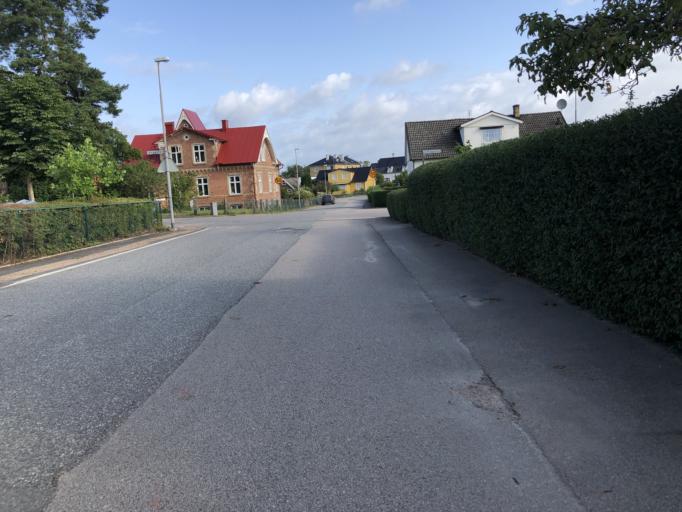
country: SE
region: Skane
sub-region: Hassleholms Kommun
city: Vinslov
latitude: 56.1020
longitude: 13.9172
